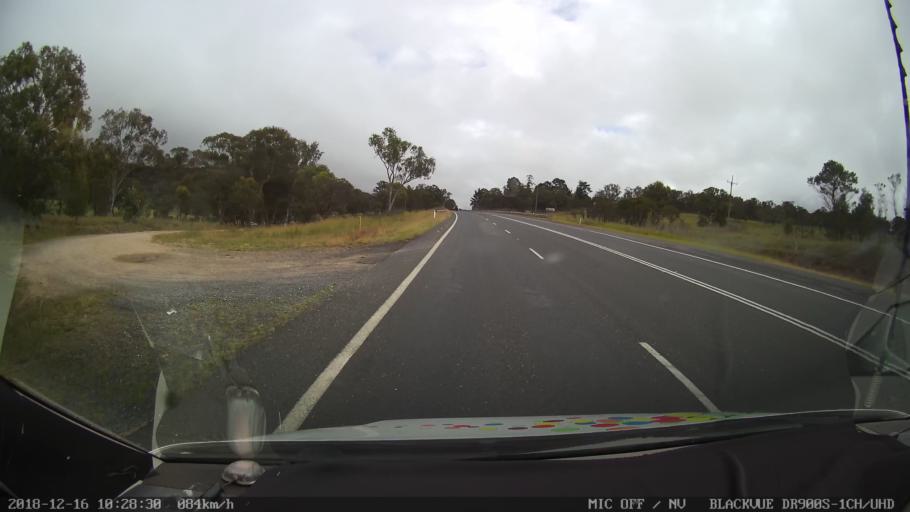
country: AU
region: New South Wales
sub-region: Tenterfield Municipality
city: Carrolls Creek
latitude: -29.1204
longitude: 151.9971
